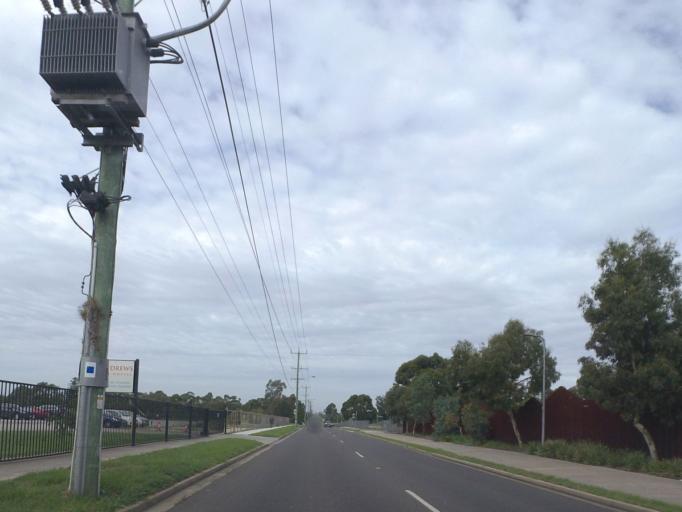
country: AU
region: Victoria
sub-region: Brimbank
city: Sunshine West
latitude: -37.7838
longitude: 144.8119
